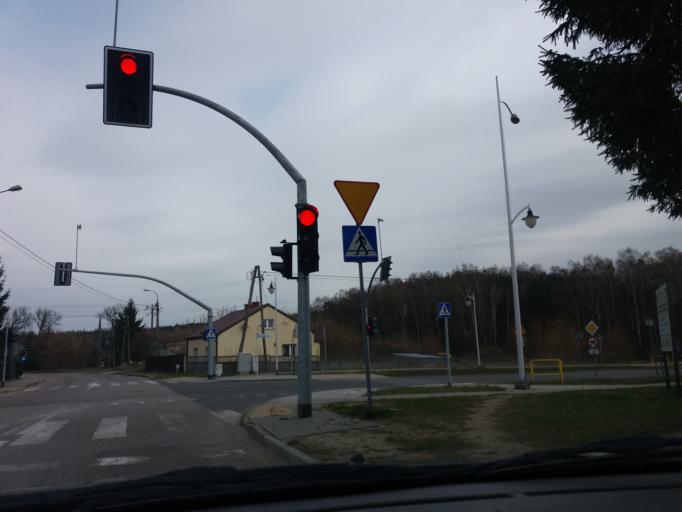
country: PL
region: Masovian Voivodeship
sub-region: Powiat mlawski
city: Mlawa
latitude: 53.1322
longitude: 20.3614
